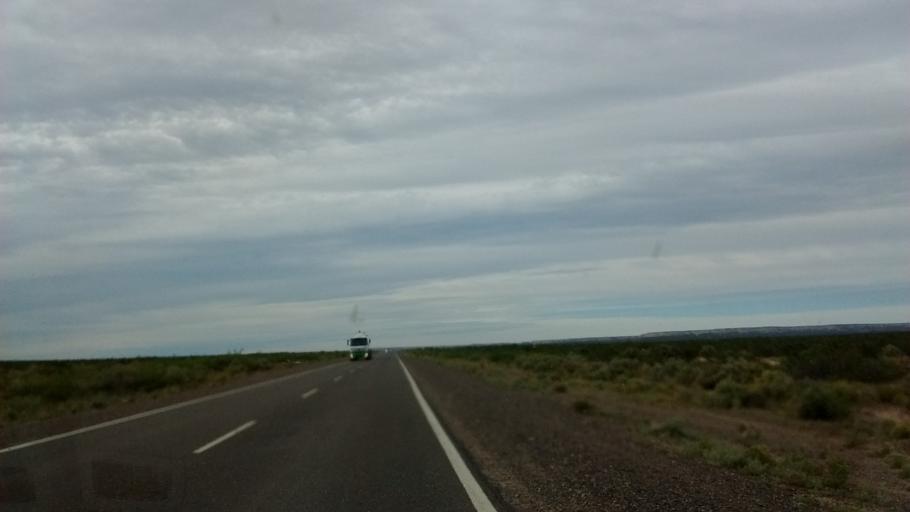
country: AR
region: Rio Negro
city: Catriel
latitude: -38.0712
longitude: -67.9232
